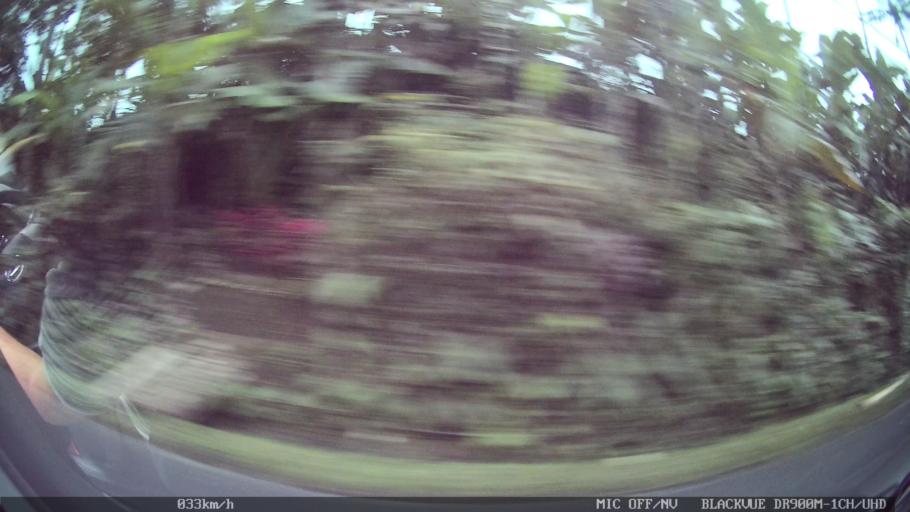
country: ID
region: Bali
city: Empalan
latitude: -8.3754
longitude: 115.1557
